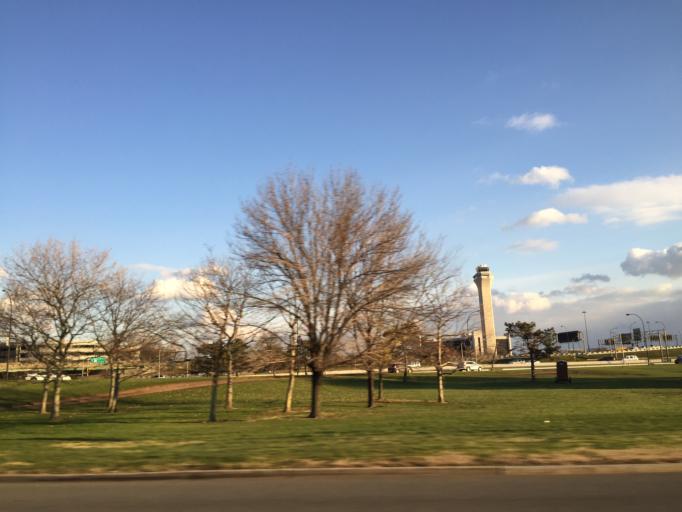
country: US
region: New Jersey
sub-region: Union County
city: Elizabeth
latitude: 40.6963
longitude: -74.1880
